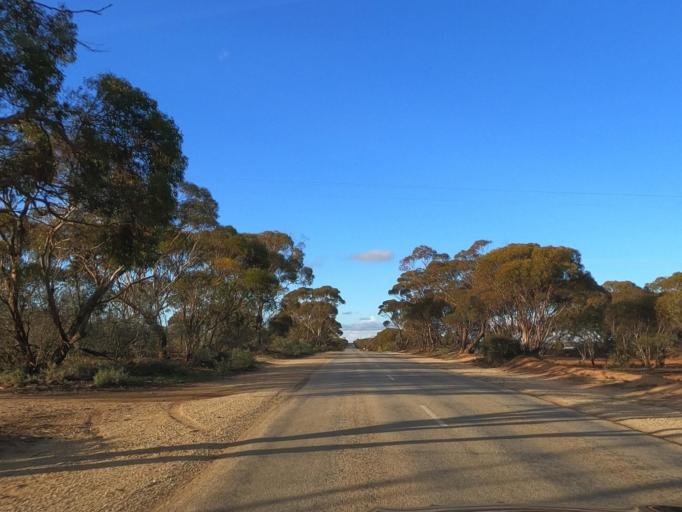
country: AU
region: Victoria
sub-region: Swan Hill
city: Swan Hill
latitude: -35.3492
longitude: 143.5131
